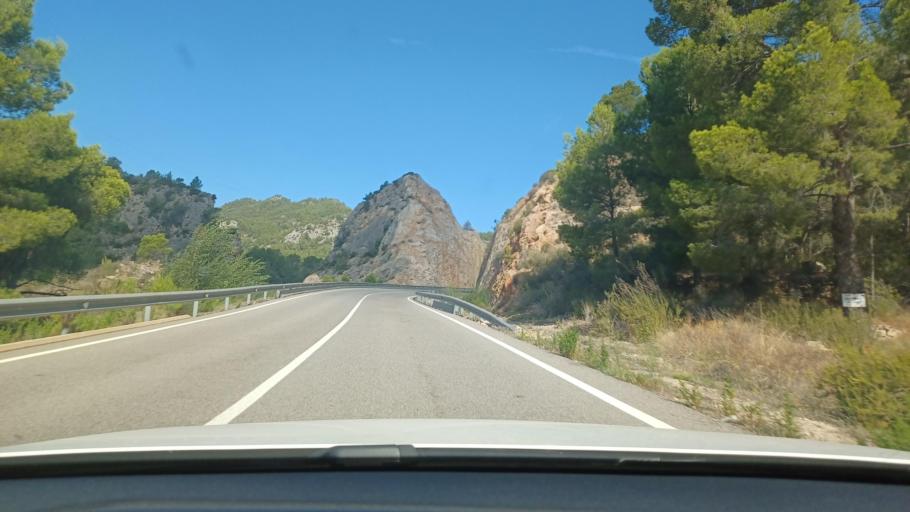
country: ES
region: Catalonia
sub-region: Provincia de Tarragona
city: Benifallet
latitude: 40.9645
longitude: 0.4470
